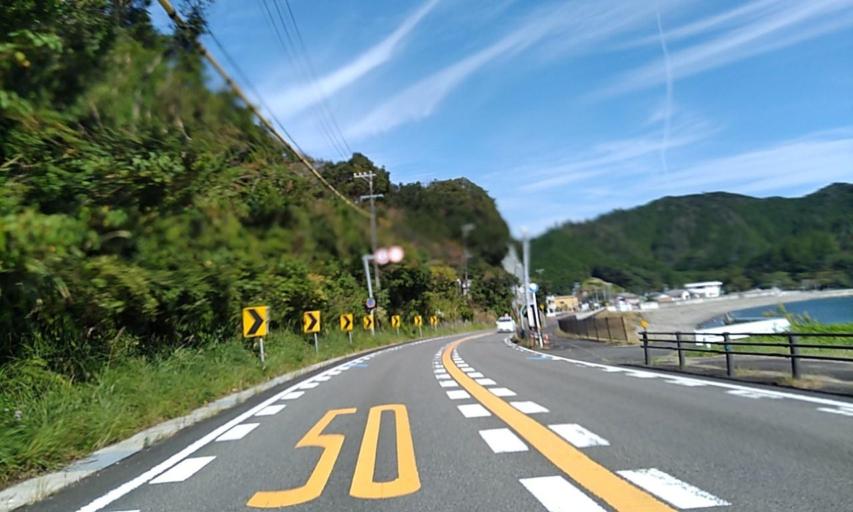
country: JP
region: Mie
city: Owase
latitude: 34.1615
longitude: 136.2777
